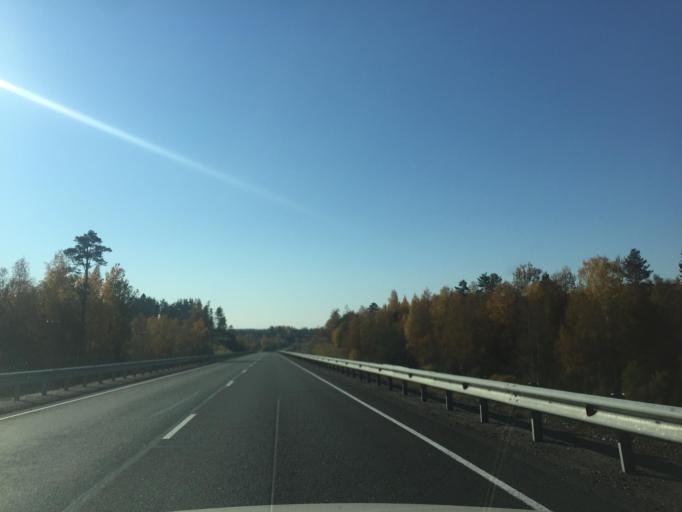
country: RU
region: Leningrad
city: Kuznechnoye
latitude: 61.3543
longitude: 29.8857
